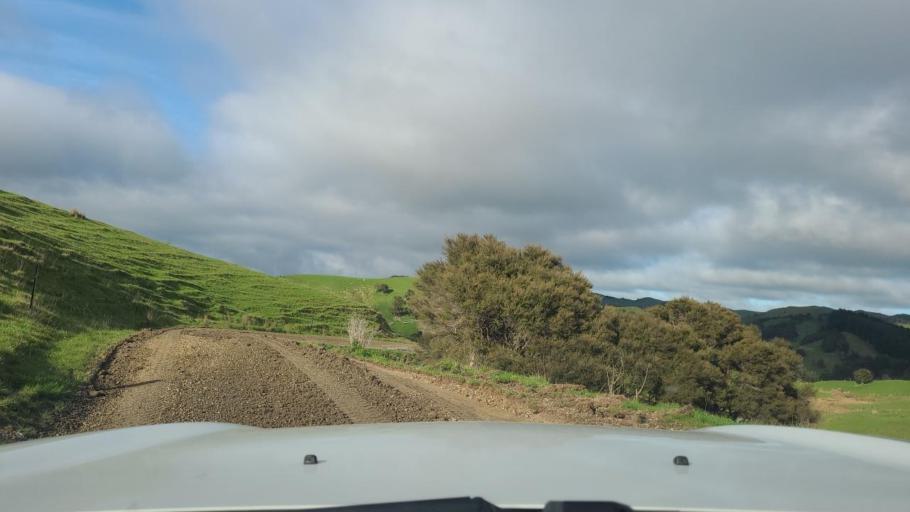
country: NZ
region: Wellington
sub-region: South Wairarapa District
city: Waipawa
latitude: -41.2305
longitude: 175.6812
